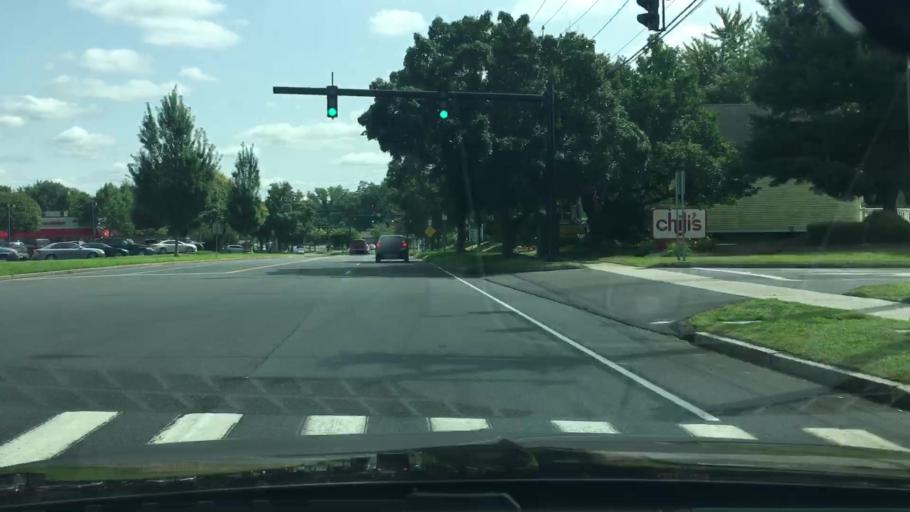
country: US
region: Connecticut
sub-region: Hartford County
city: Glastonbury
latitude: 41.7214
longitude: -72.6147
